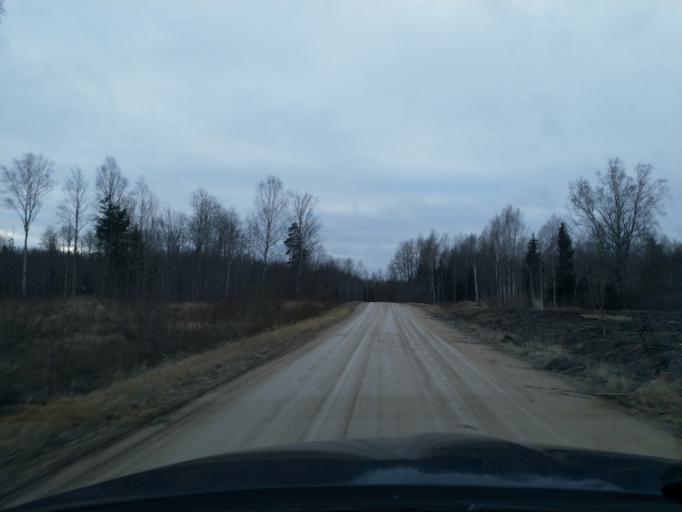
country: LV
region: Kuldigas Rajons
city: Kuldiga
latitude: 56.9115
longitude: 22.2679
